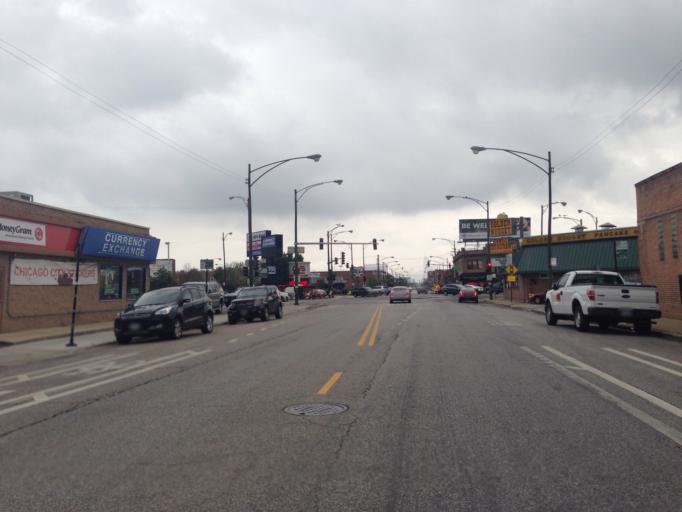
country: US
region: Illinois
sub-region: Cook County
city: Lincolnwood
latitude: 41.9328
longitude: -87.6888
